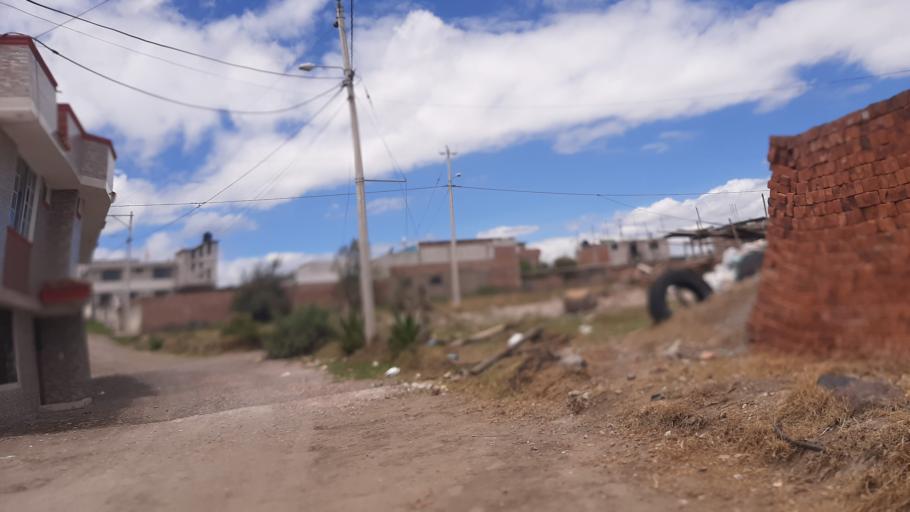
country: EC
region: Chimborazo
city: Riobamba
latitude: -1.6531
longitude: -78.6328
